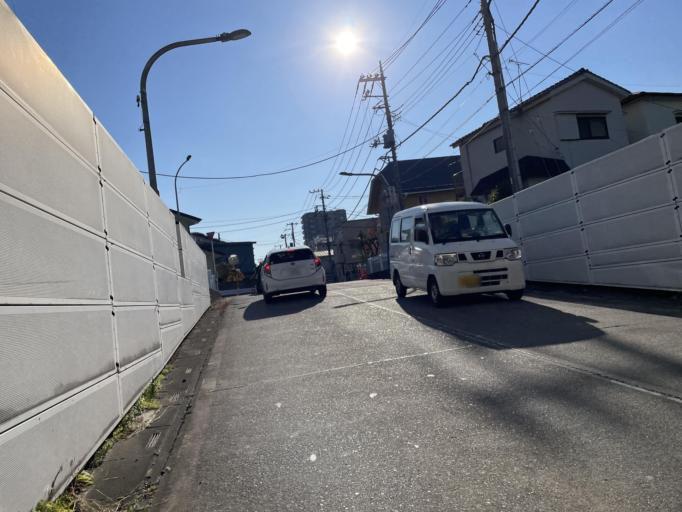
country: JP
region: Saitama
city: Soka
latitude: 35.8106
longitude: 139.7985
